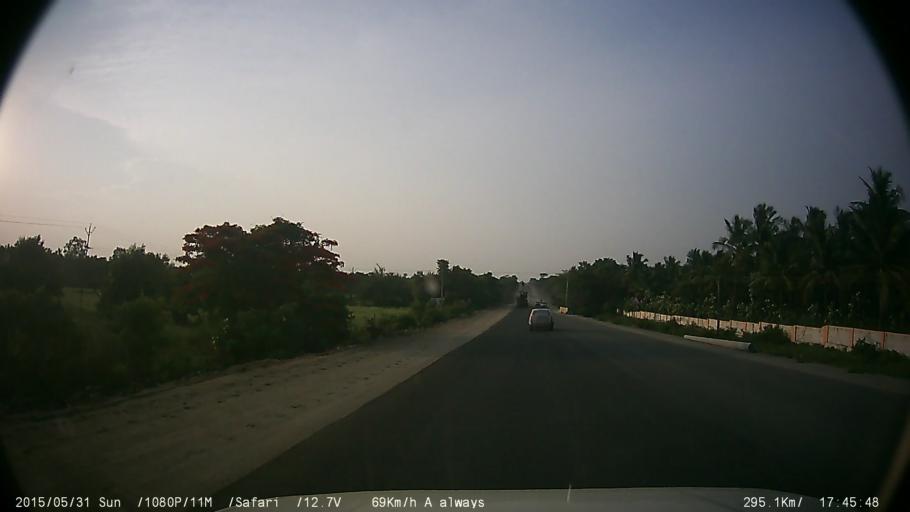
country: IN
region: Karnataka
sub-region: Chamrajnagar
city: Gundlupet
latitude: 11.9537
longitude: 76.6706
